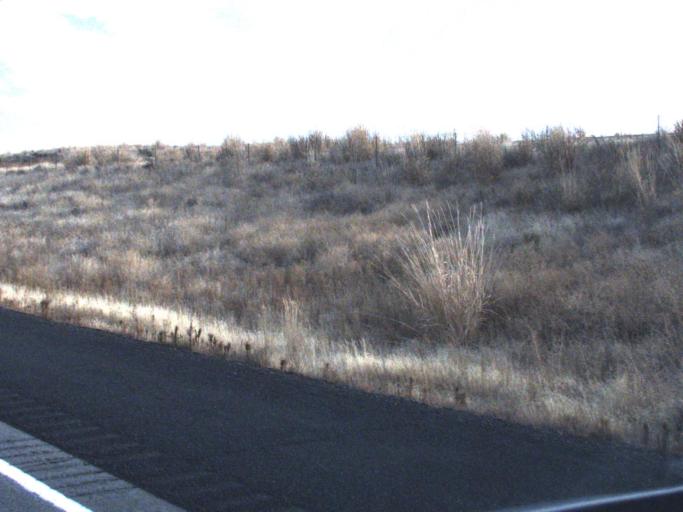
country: US
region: Washington
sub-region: Franklin County
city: Connell
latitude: 46.8508
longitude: -118.6397
